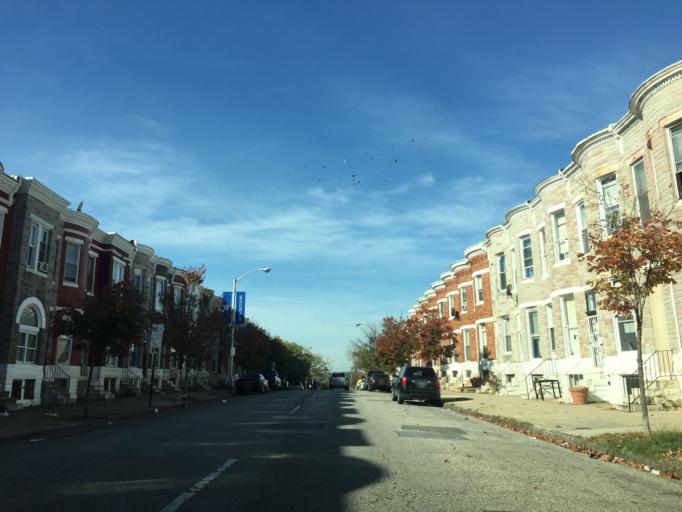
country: US
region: Maryland
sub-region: City of Baltimore
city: Baltimore
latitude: 39.2895
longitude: -76.6472
